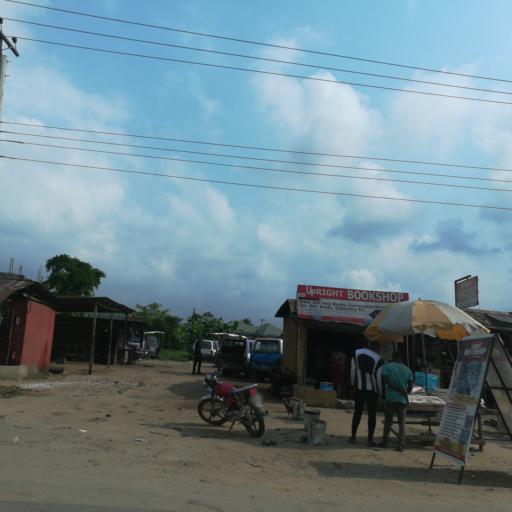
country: NG
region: Rivers
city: Okrika
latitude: 4.7810
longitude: 7.1237
